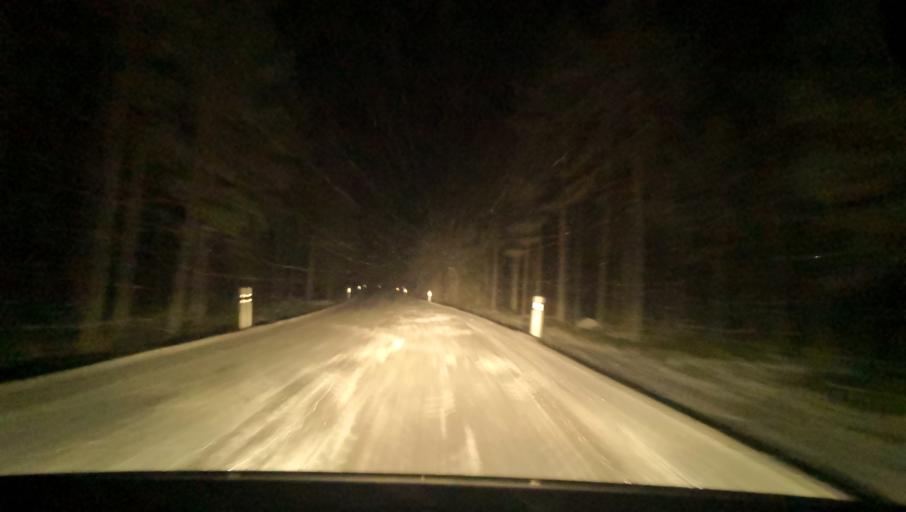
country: SE
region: Uppsala
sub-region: Heby Kommun
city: Tarnsjo
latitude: 60.1170
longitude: 16.8845
